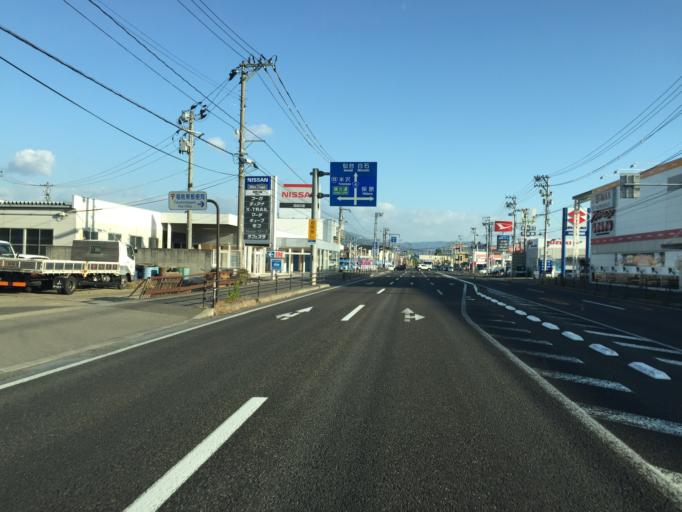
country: JP
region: Fukushima
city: Fukushima-shi
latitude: 37.7960
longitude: 140.4893
